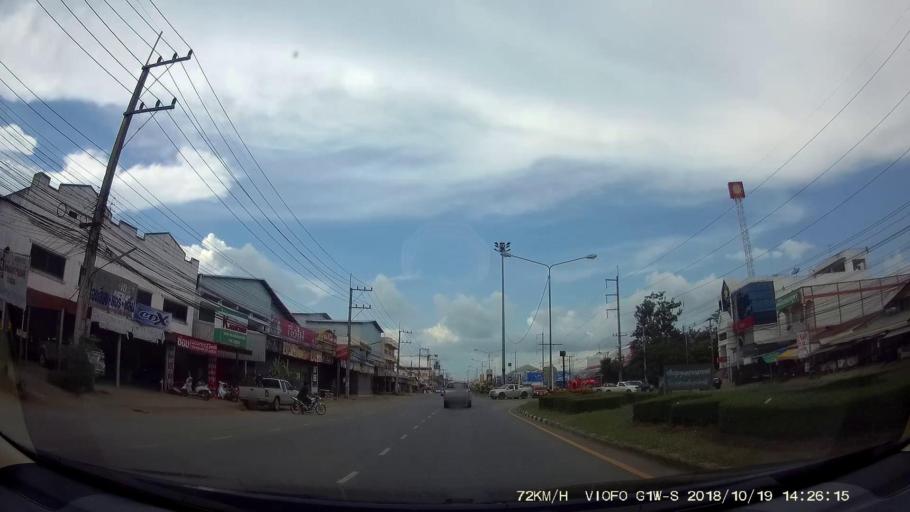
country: TH
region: Chaiyaphum
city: Kaeng Khro
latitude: 16.1045
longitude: 102.2605
